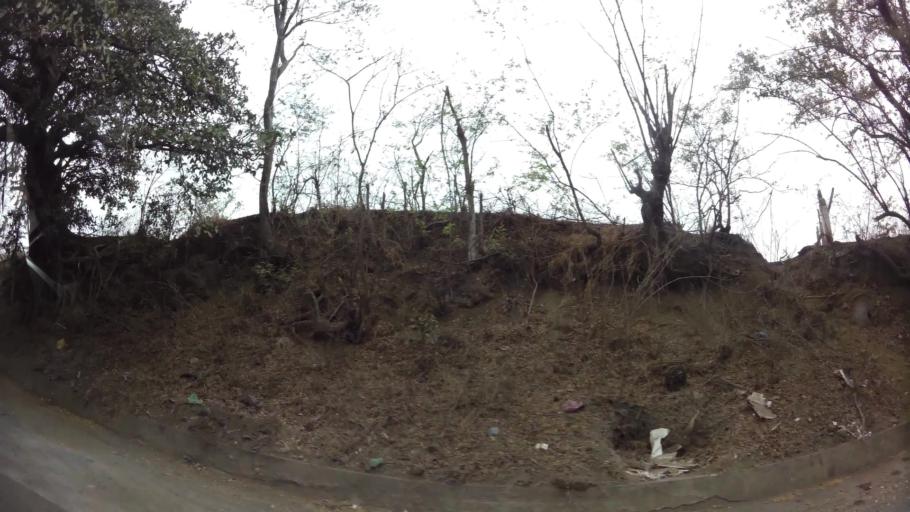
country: NI
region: Masaya
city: Ticuantepe
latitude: 12.0769
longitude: -86.1808
